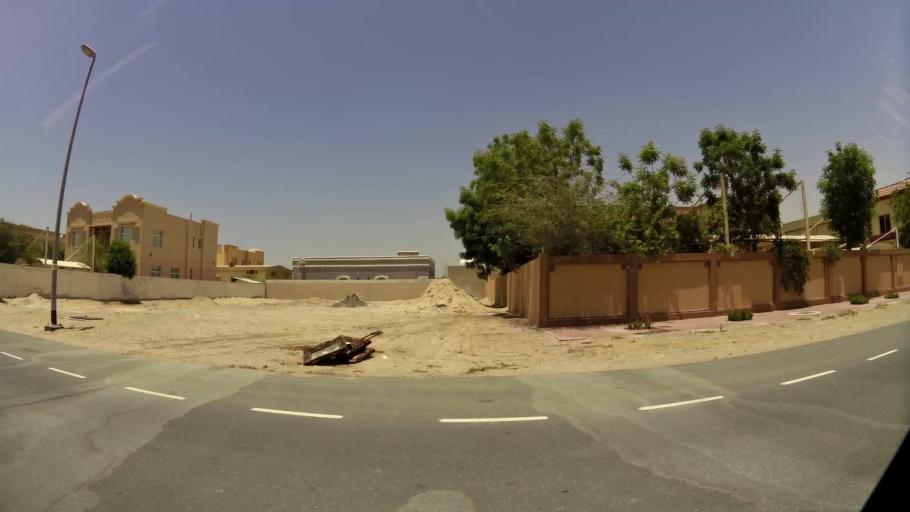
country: AE
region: Dubai
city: Dubai
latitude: 25.0901
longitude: 55.1923
